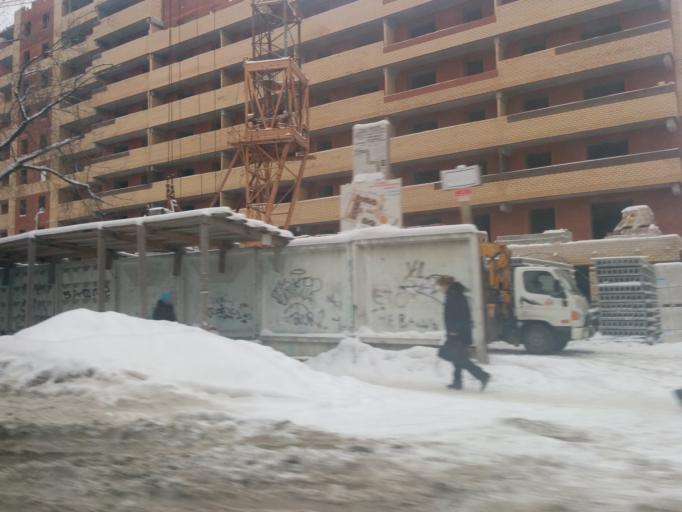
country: RU
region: Perm
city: Kondratovo
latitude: 58.0300
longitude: 56.0181
